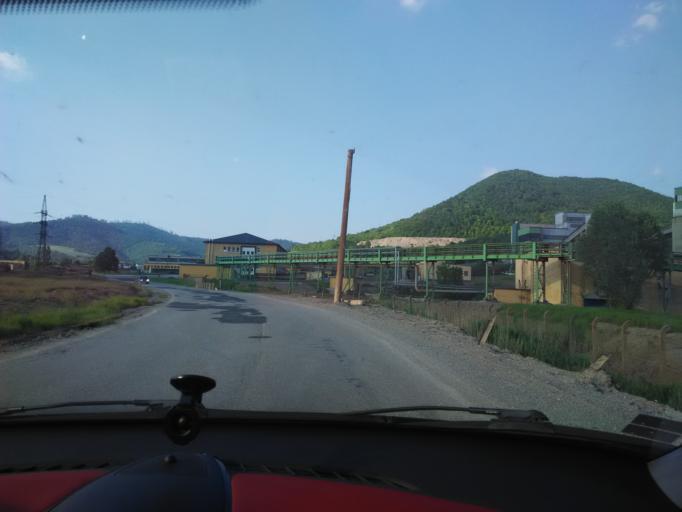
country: SK
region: Banskobystricky
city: Revuca
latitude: 48.6482
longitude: 20.2200
